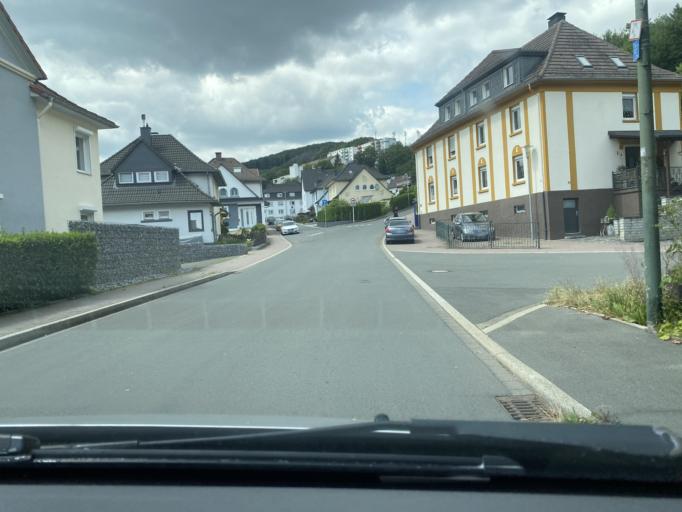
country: DE
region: North Rhine-Westphalia
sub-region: Regierungsbezirk Arnsberg
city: Luedenscheid
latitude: 51.2564
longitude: 7.6268
